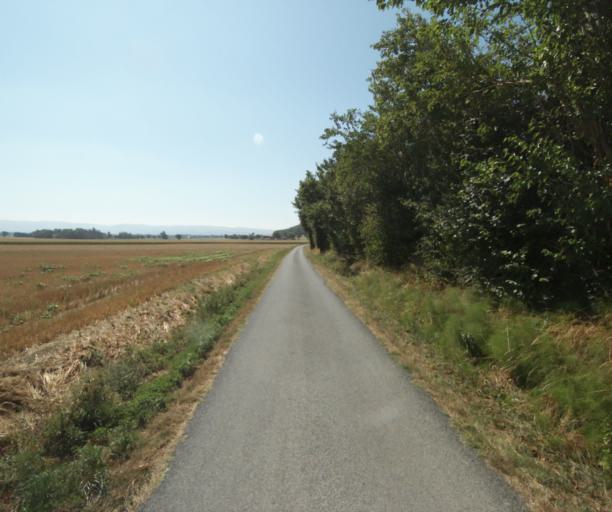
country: FR
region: Midi-Pyrenees
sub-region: Departement du Tarn
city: Puylaurens
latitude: 43.5253
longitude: 1.9412
